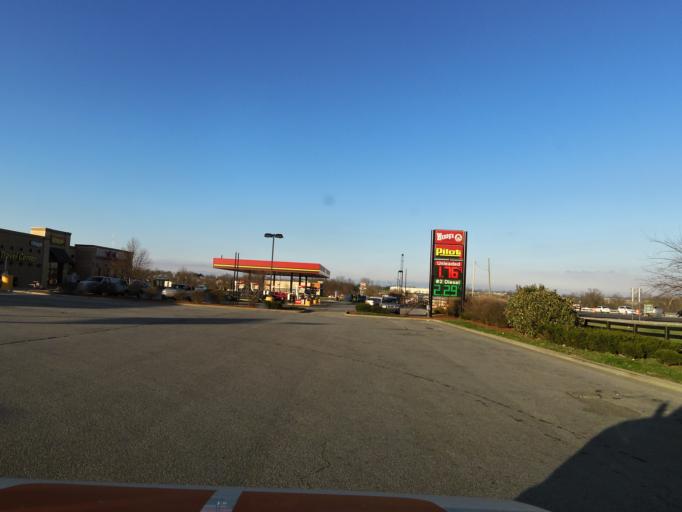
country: US
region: Kentucky
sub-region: Shelby County
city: Simpsonville
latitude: 38.2097
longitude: -85.3477
